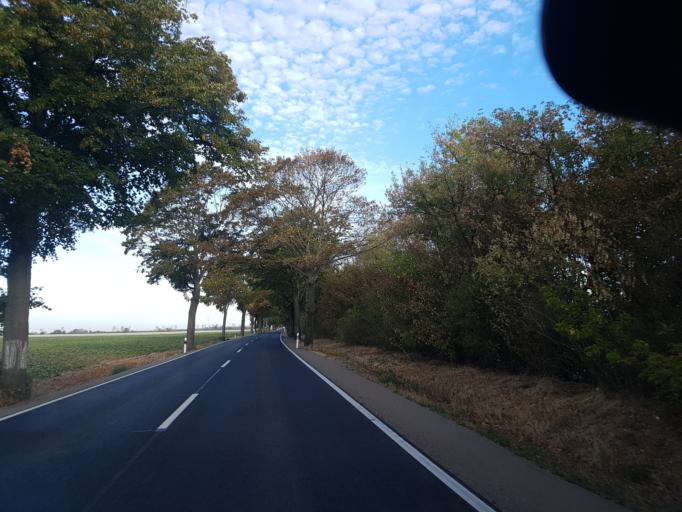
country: DE
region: Brandenburg
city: Ihlow
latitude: 51.9111
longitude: 13.2420
